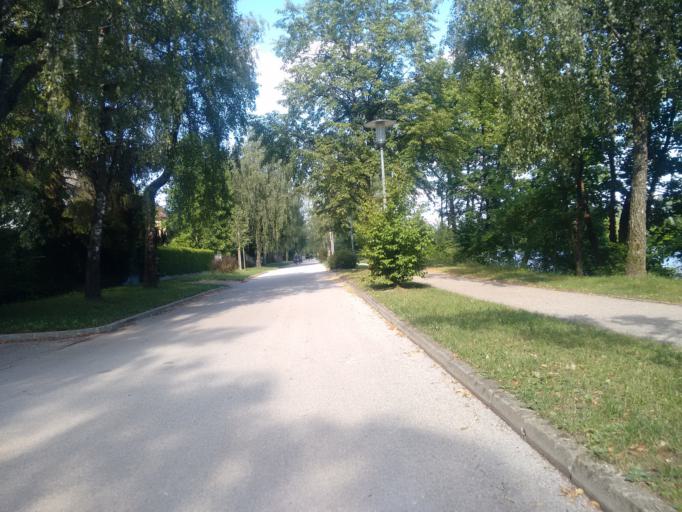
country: AT
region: Upper Austria
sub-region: Wels-Land
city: Thalheim bei Wels
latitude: 48.1556
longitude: 14.0324
